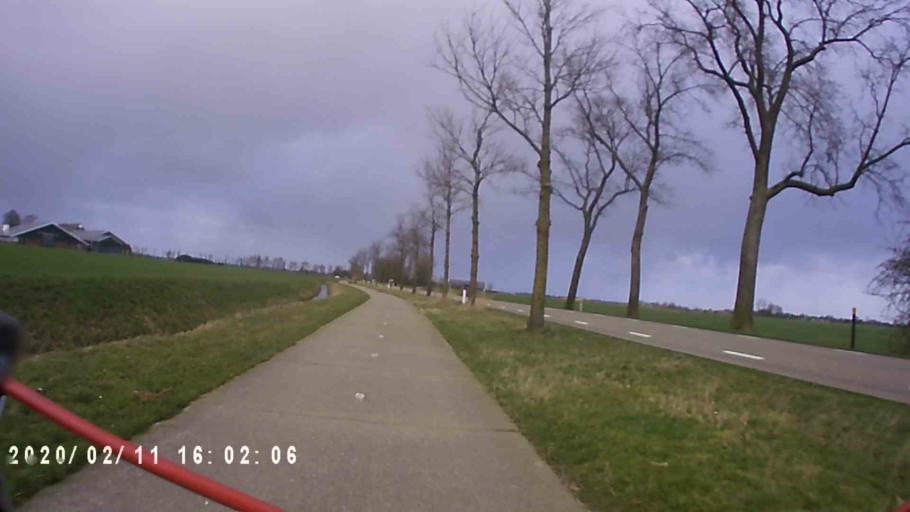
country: NL
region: Groningen
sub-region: Gemeente Zuidhorn
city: Oldehove
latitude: 53.2979
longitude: 6.4208
